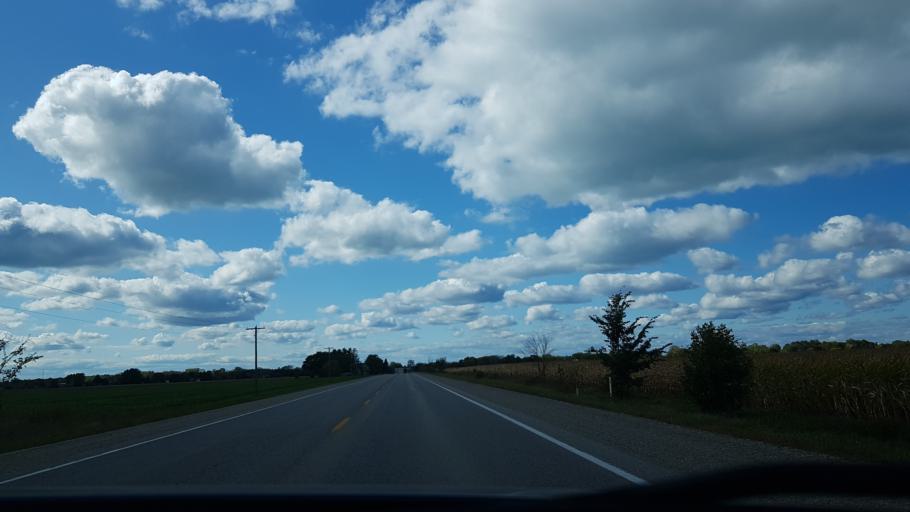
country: CA
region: Ontario
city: Bluewater
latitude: 43.3369
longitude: -81.7226
